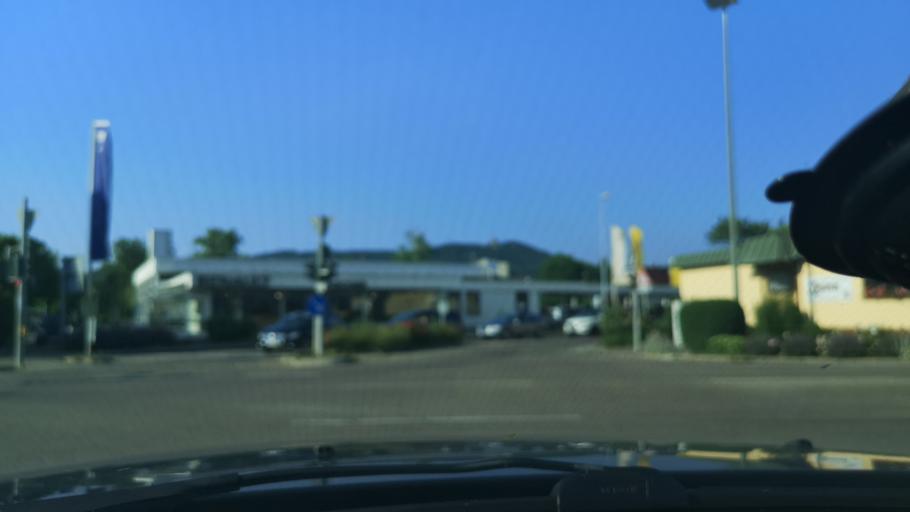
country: DE
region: Baden-Wuerttemberg
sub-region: Regierungsbezirk Stuttgart
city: Sussen
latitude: 48.6778
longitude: 9.7517
